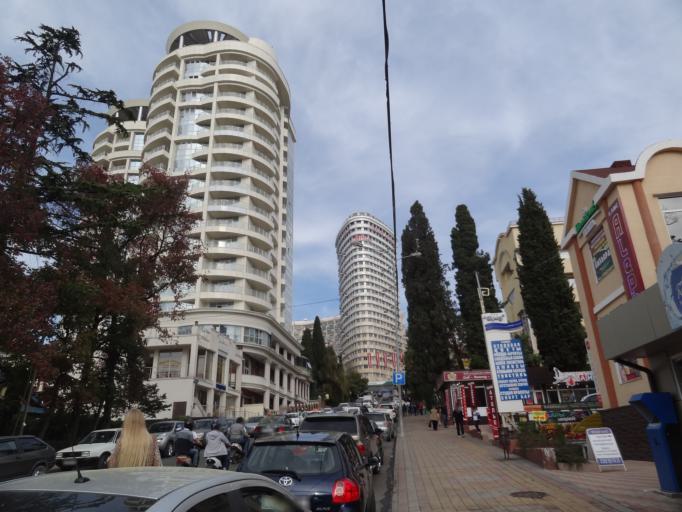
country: RU
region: Krasnodarskiy
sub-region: Sochi City
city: Sochi
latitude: 43.5779
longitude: 39.7279
